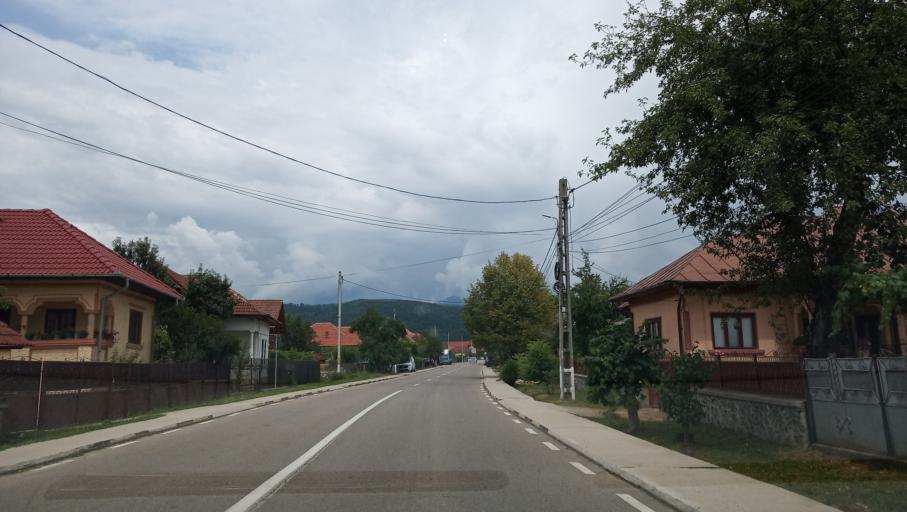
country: RO
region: Gorj
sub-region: Comuna Tismana
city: Tismana
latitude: 45.0543
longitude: 22.9457
